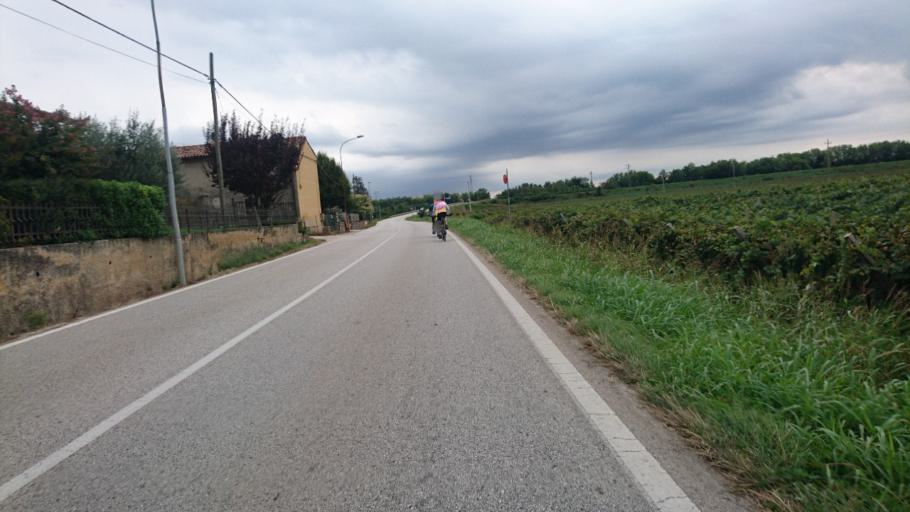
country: IT
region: Veneto
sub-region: Provincia di Vicenza
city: Gambellara
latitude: 45.4429
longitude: 11.3551
